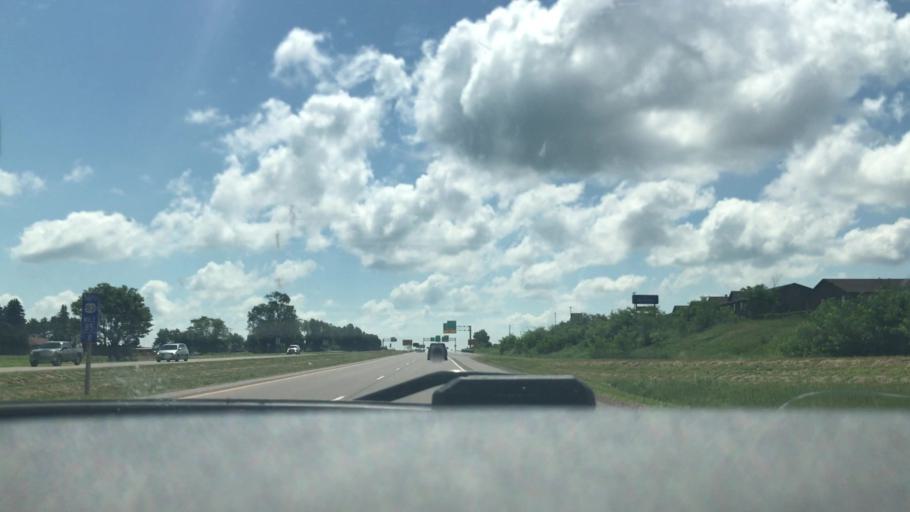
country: US
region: Wisconsin
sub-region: Eau Claire County
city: Altoona
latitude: 44.7768
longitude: -91.4347
